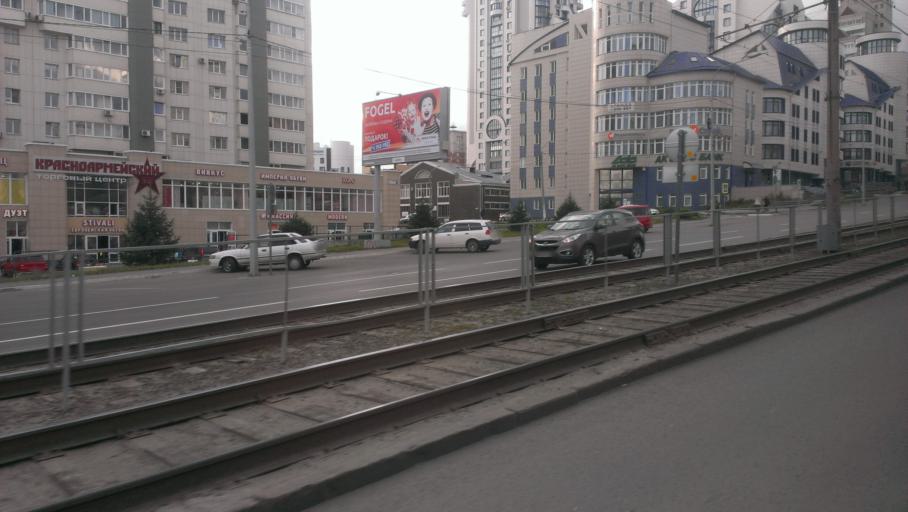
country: RU
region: Altai Krai
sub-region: Gorod Barnaulskiy
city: Barnaul
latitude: 53.3396
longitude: 83.7724
